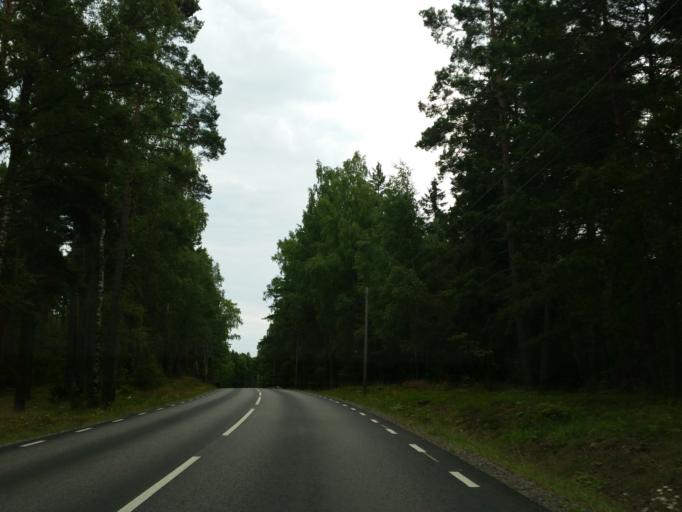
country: SE
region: Stockholm
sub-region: Botkyrka Kommun
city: Eriksberg
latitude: 59.2324
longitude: 17.7817
